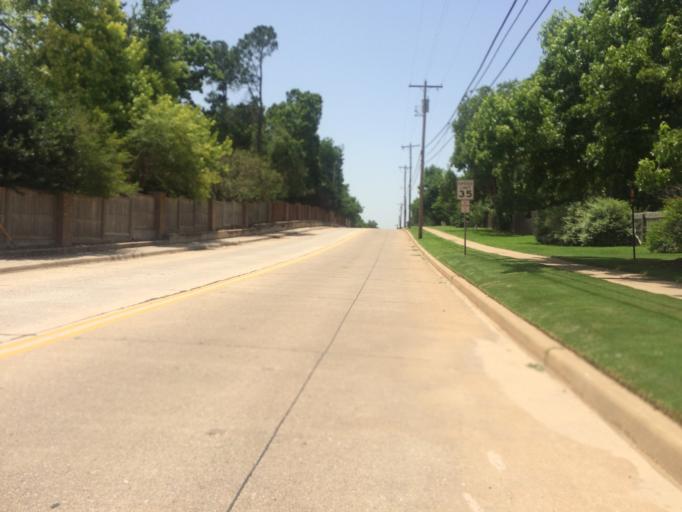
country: US
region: Oklahoma
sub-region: Cleveland County
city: Norman
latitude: 35.1894
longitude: -97.4604
